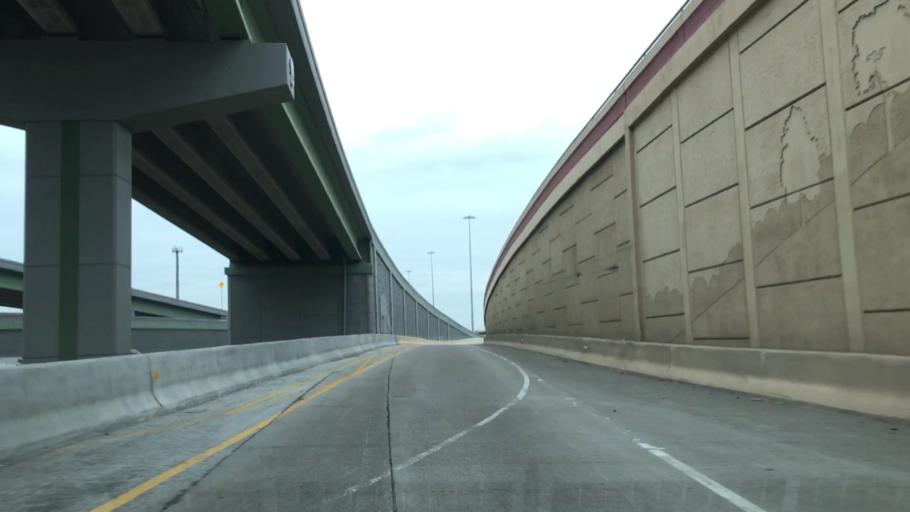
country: US
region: Texas
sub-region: Dallas County
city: Irving
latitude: 32.8410
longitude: -96.9142
